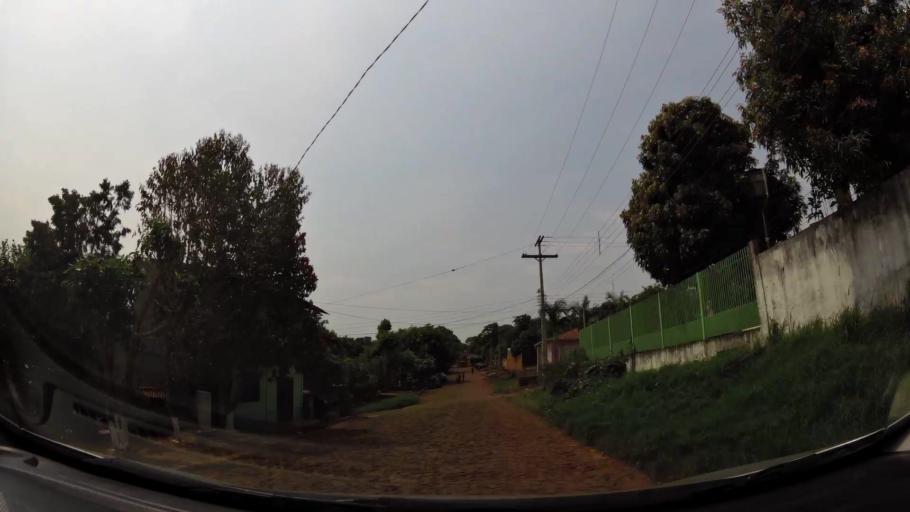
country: BR
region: Parana
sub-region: Foz Do Iguacu
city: Foz do Iguacu
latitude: -25.5702
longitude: -54.6162
